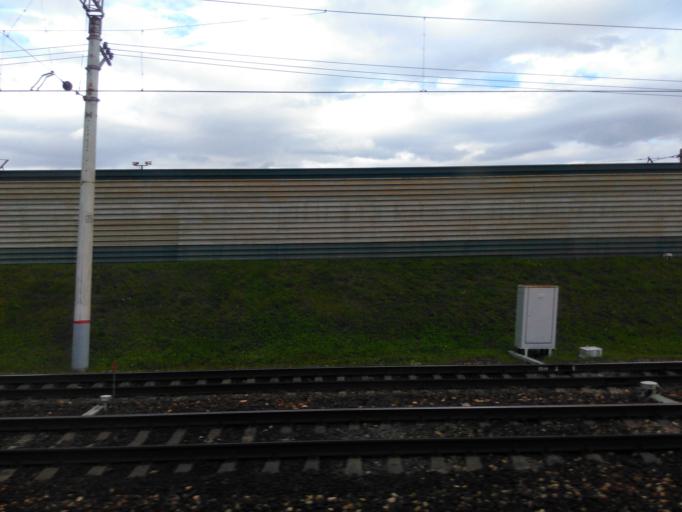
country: RU
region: Moscow
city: Rostokino
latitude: 55.8501
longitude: 37.6720
